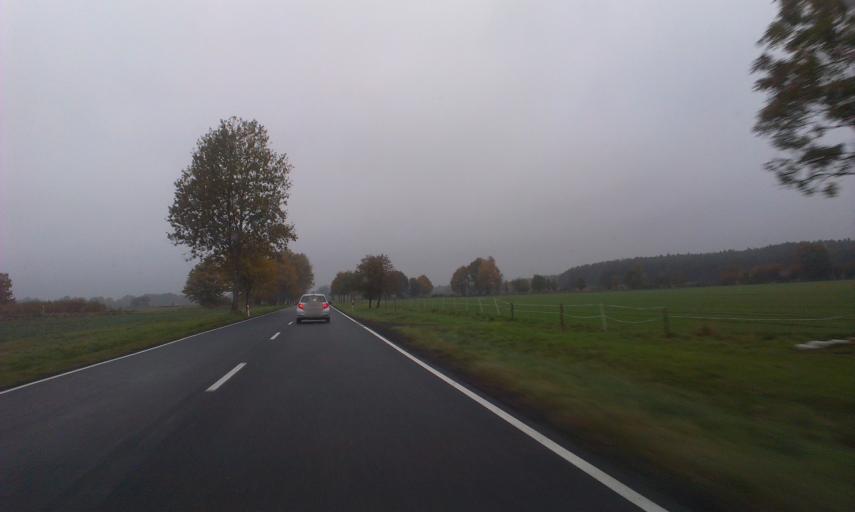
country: PL
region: West Pomeranian Voivodeship
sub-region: Powiat koszalinski
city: Bobolice
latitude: 54.0185
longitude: 16.4860
